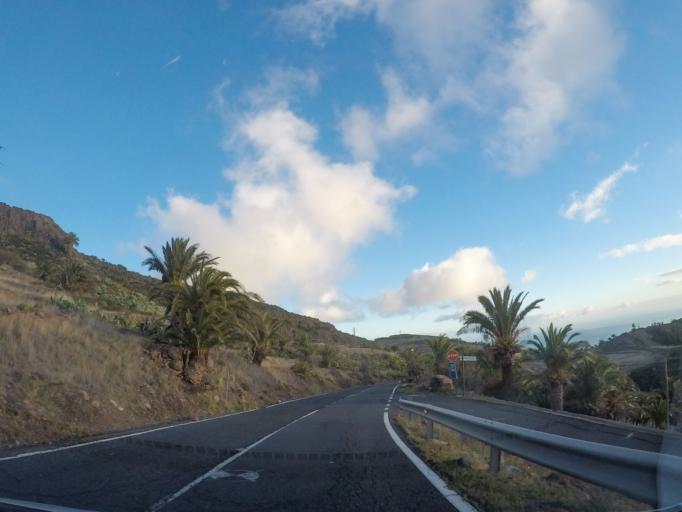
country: ES
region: Canary Islands
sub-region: Provincia de Santa Cruz de Tenerife
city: Alajero
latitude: 28.0752
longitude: -17.2392
